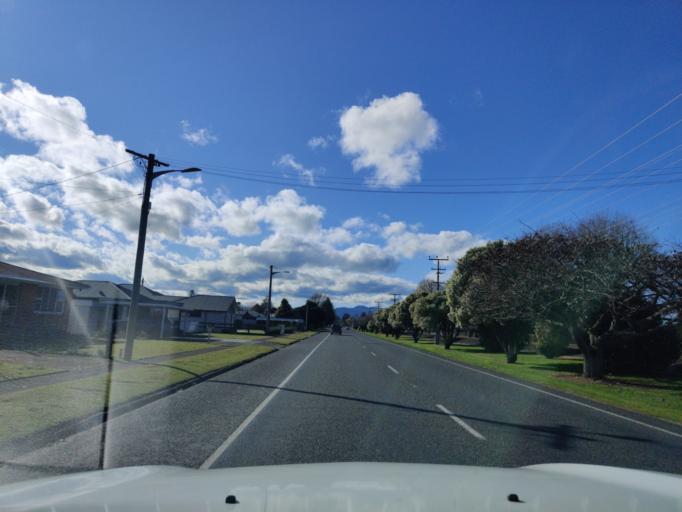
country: NZ
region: Waikato
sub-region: Matamata-Piako District
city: Matamata
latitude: -37.8291
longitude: 175.7683
